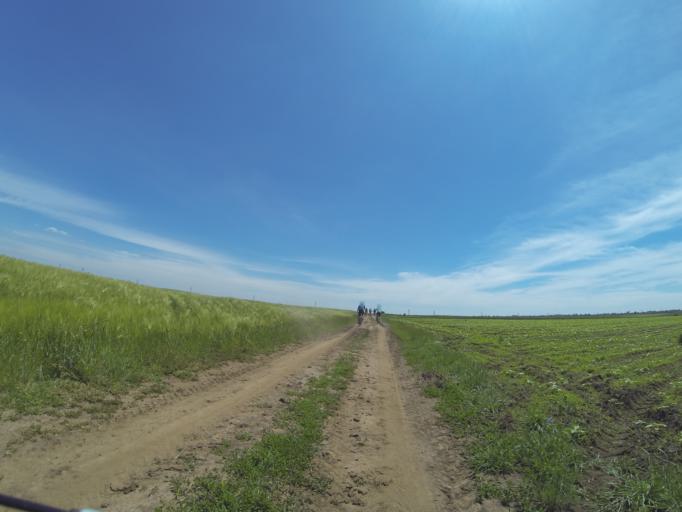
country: RO
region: Dolj
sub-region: Comuna Leu
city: Zanoaga
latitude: 44.1762
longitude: 24.0889
